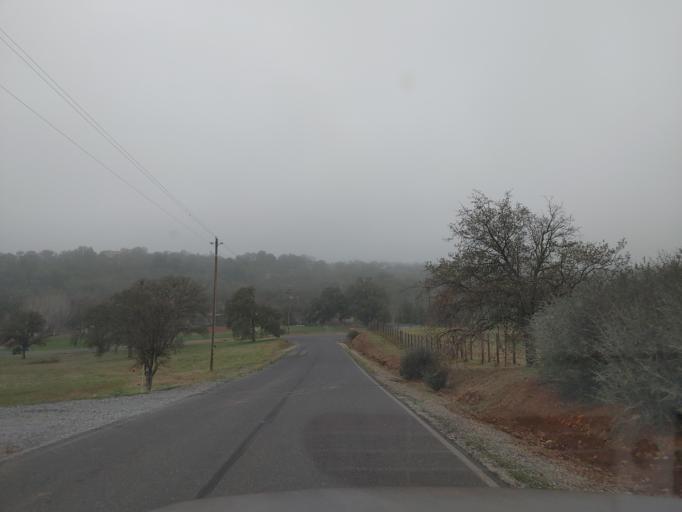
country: US
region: California
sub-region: Calaveras County
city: Copperopolis
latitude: 37.9407
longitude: -120.6188
